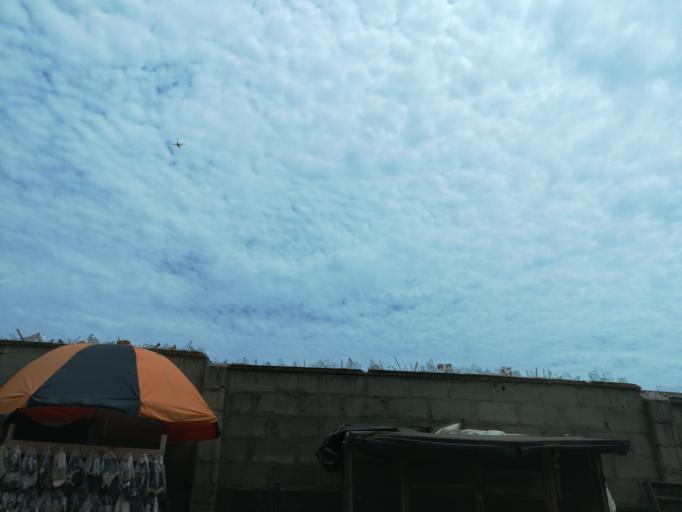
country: NG
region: Lagos
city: Oshodi
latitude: 6.5599
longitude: 3.3295
